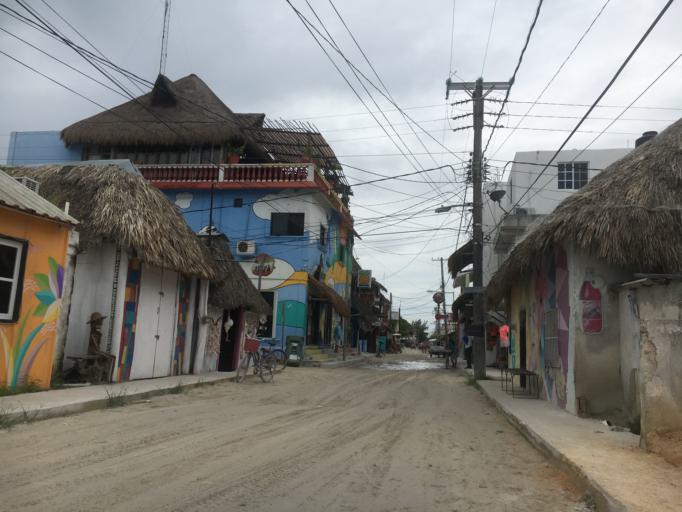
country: MX
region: Quintana Roo
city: Kantunilkin
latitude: 21.5250
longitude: -87.3783
